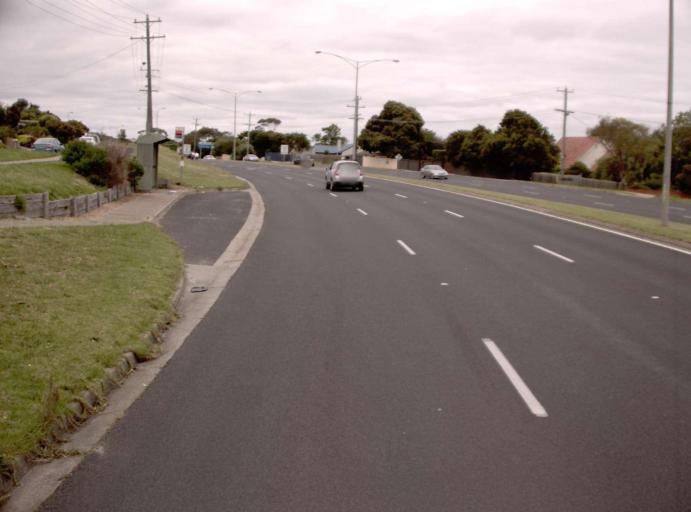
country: AU
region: Victoria
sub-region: Mornington Peninsula
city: Mornington
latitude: -38.2370
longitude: 145.0360
